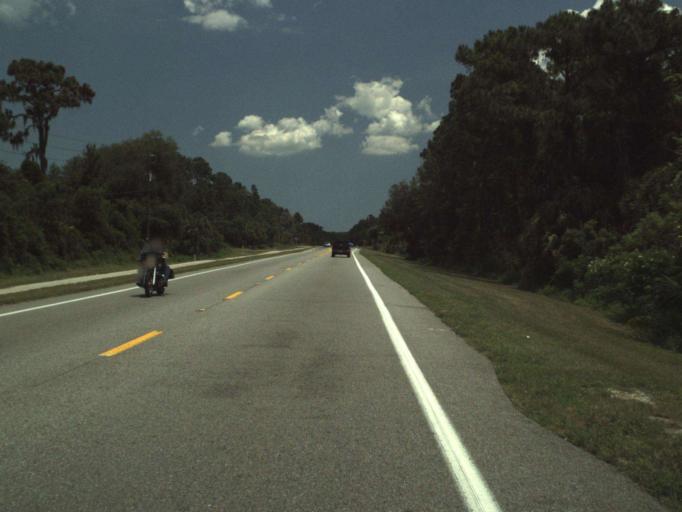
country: US
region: Florida
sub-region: Brevard County
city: Titusville
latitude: 28.5988
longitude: -80.8409
